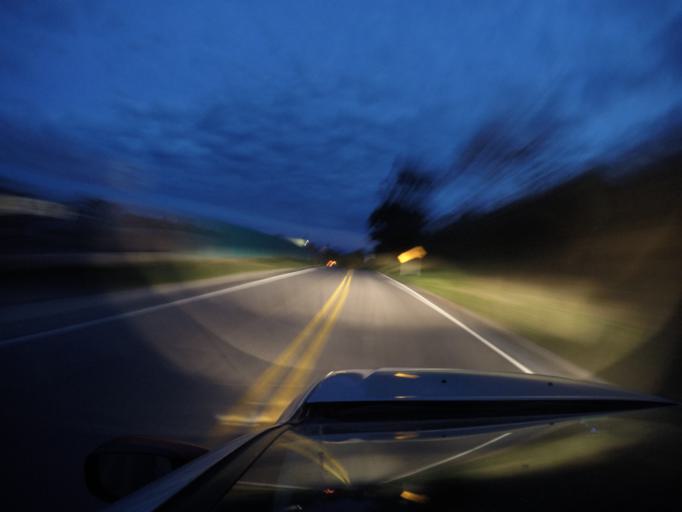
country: CO
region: Tolima
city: Fresno
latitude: 5.1570
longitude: -75.0737
